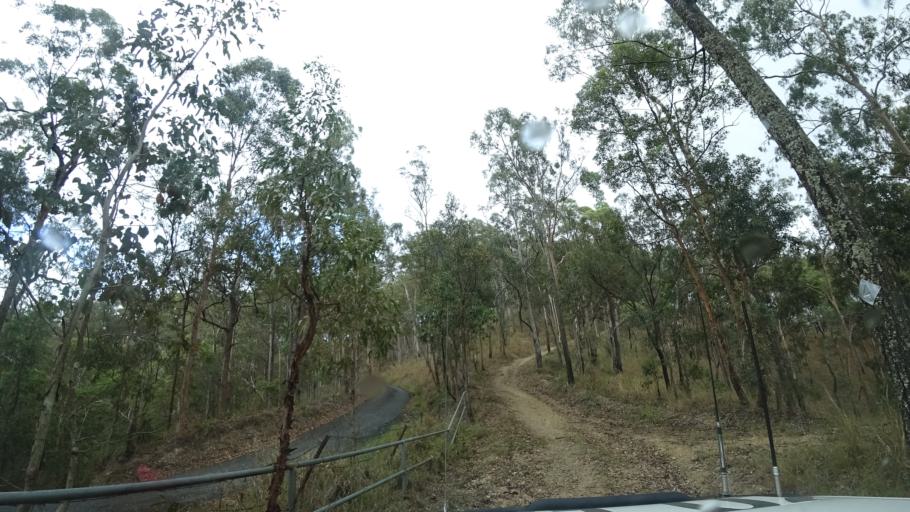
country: AU
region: Queensland
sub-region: Brisbane
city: Pullenvale
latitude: -27.4621
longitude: 152.8530
